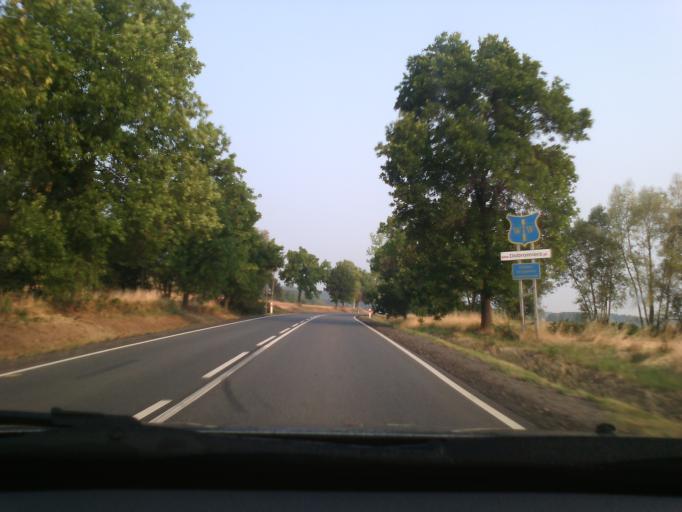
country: PL
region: Lower Silesian Voivodeship
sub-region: Powiat swidnicki
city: Swiebodzice
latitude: 50.8804
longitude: 16.2759
